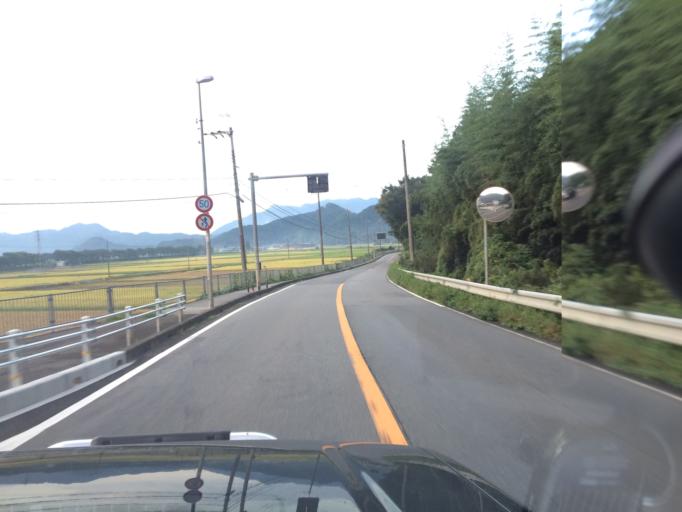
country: JP
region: Hyogo
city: Nishiwaki
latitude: 35.1343
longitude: 135.0191
